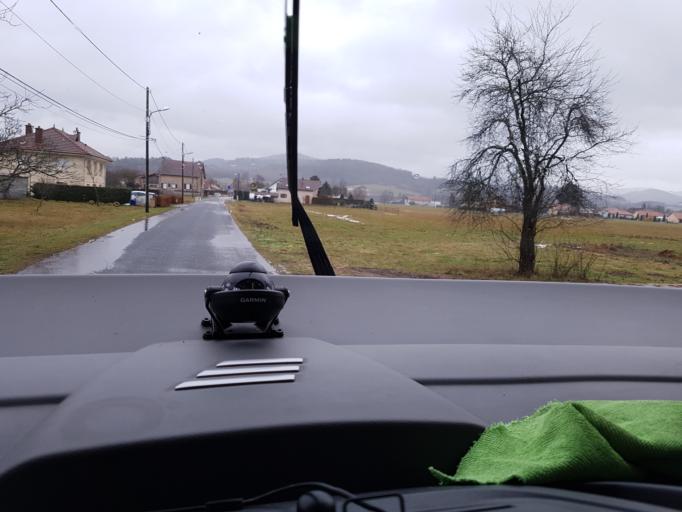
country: FR
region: Lorraine
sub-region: Departement des Vosges
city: Saint-Leonard
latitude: 48.2061
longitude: 6.9371
